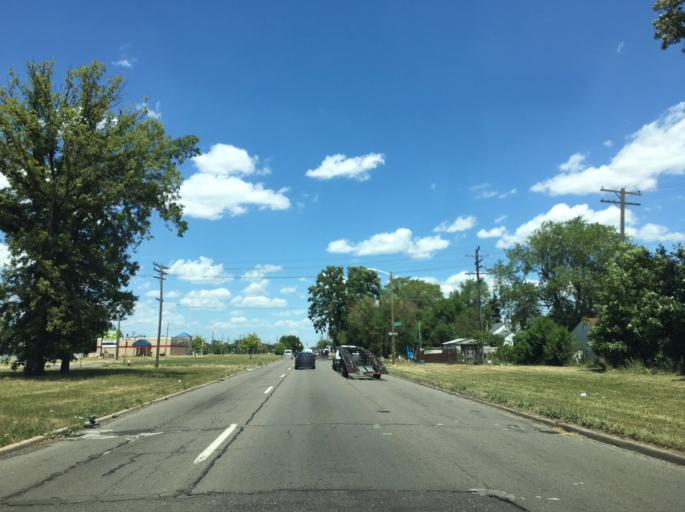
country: US
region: Michigan
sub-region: Macomb County
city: Warren
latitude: 42.4379
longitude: -83.0436
